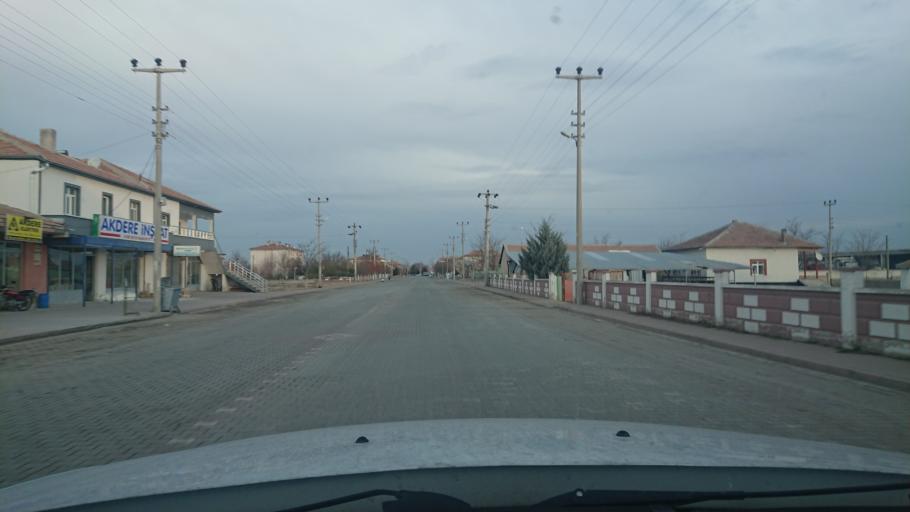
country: TR
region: Aksaray
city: Yesilova
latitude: 38.3389
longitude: 33.7507
